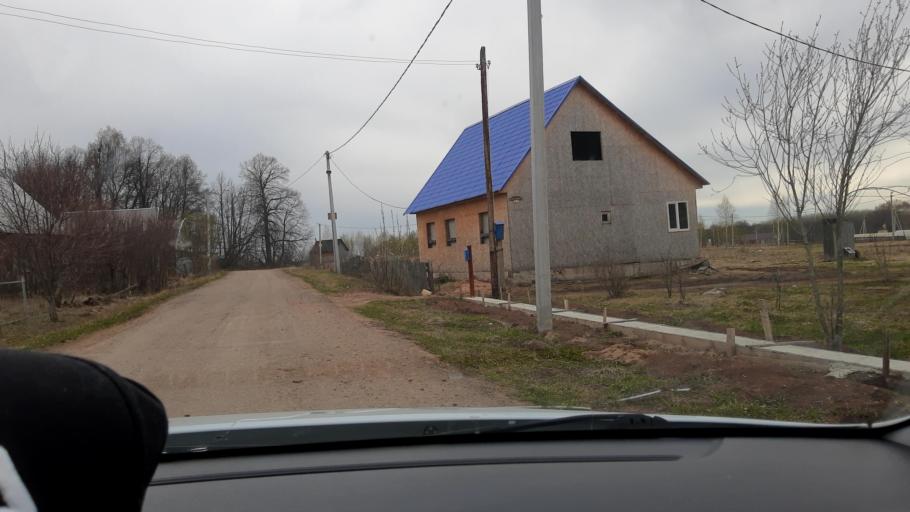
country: RU
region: Bashkortostan
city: Iglino
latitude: 54.7693
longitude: 56.5247
